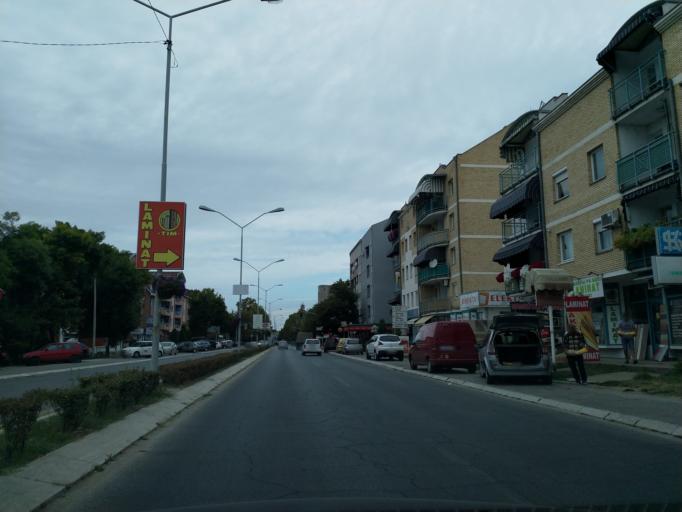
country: RS
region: Central Serbia
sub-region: Pomoravski Okrug
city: Jagodina
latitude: 43.9699
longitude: 21.2710
